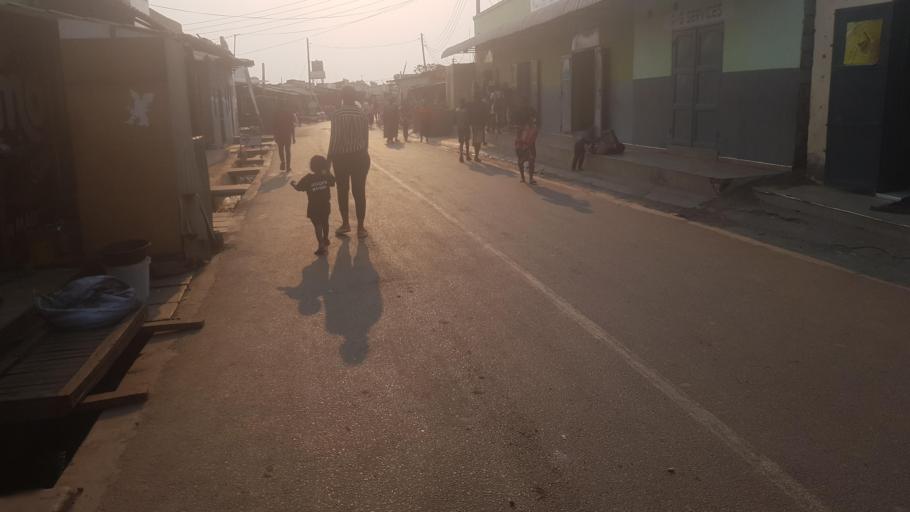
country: ZM
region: Lusaka
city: Lusaka
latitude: -15.4454
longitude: 28.3807
